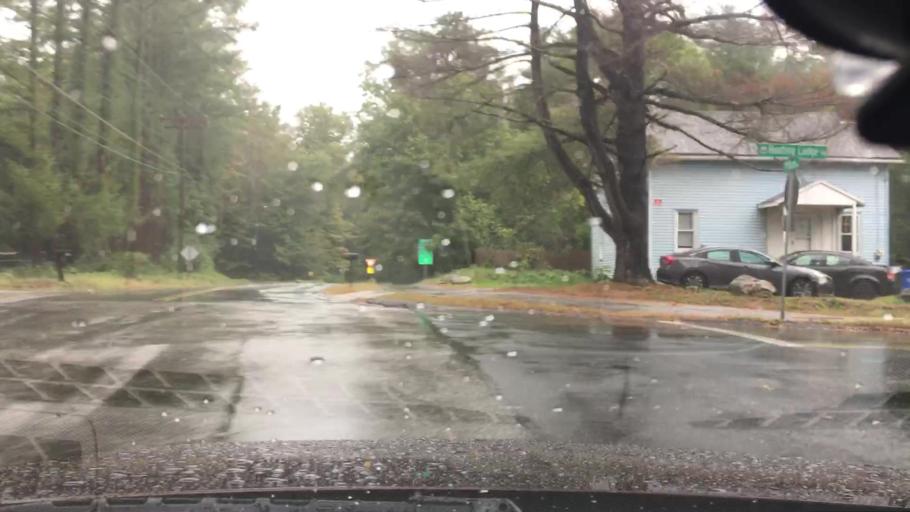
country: US
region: Connecticut
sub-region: Tolland County
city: Storrs
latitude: 41.8170
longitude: -72.2826
